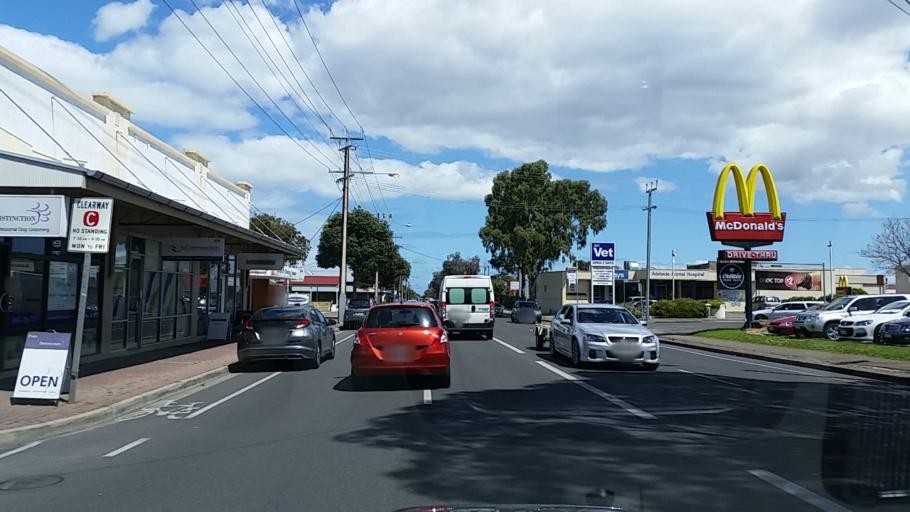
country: AU
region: South Australia
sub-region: Norwood Payneham St Peters
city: Trinity Gardens
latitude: -34.9146
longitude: 138.6458
